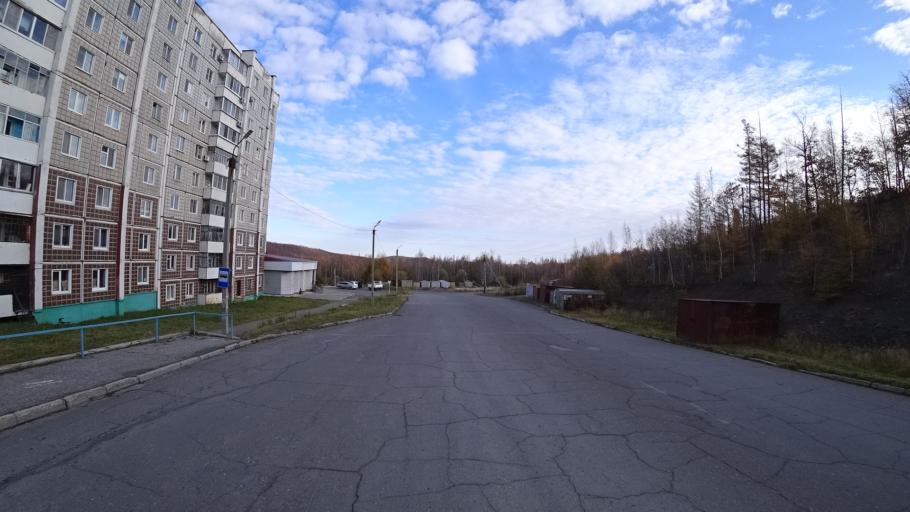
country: RU
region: Khabarovsk Krai
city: Amursk
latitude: 50.2478
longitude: 136.9226
